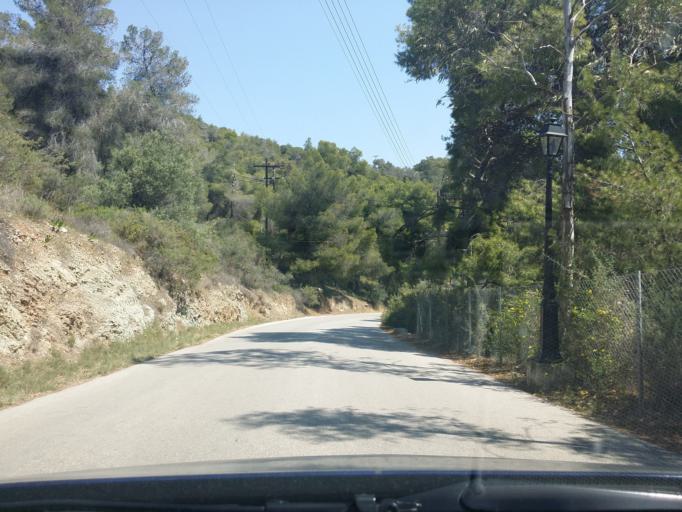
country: GR
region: Attica
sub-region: Nomos Piraios
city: Poros
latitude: 37.5078
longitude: 23.4477
